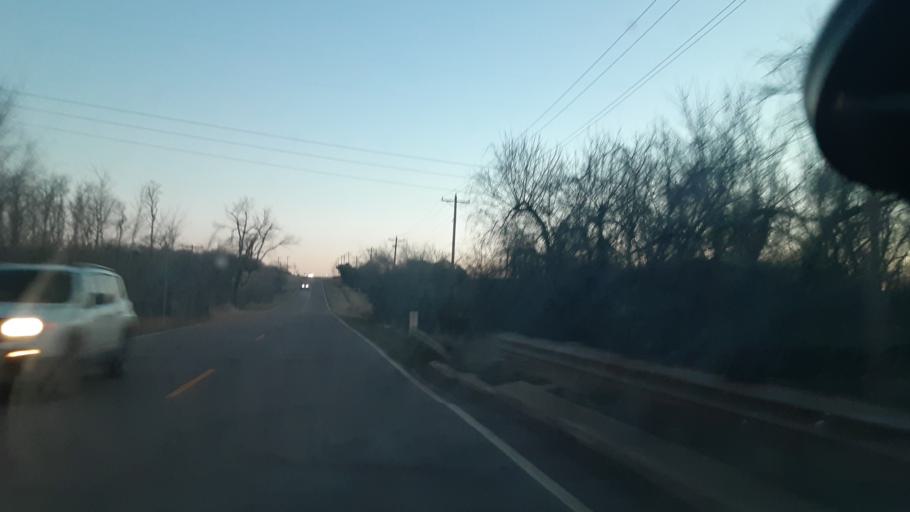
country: US
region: Oklahoma
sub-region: Oklahoma County
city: Edmond
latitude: 35.6899
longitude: -97.4251
